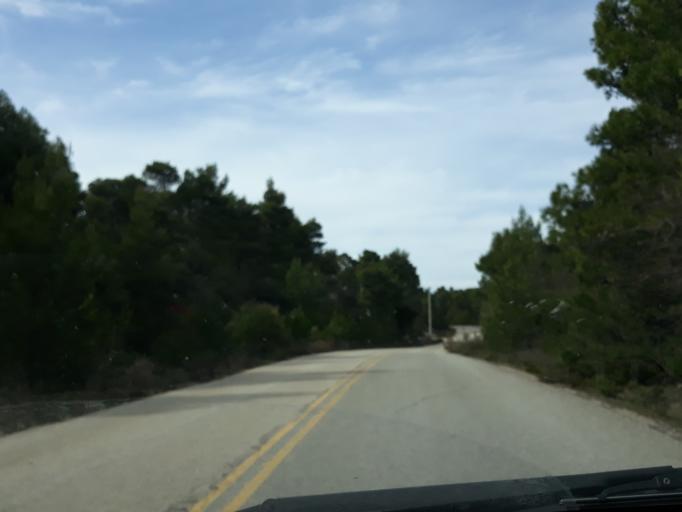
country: GR
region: Attica
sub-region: Nomarchia Anatolikis Attikis
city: Afidnes
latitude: 38.2109
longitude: 23.7989
